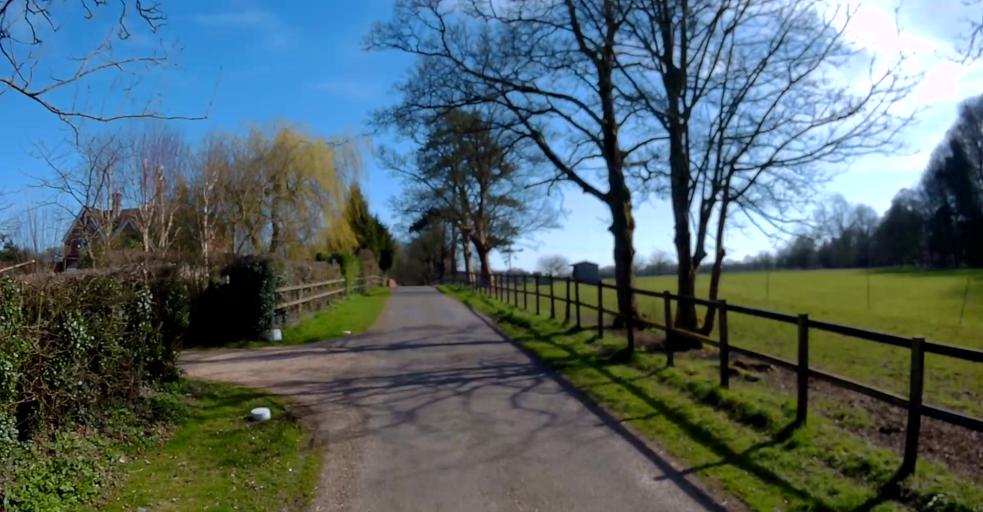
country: GB
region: England
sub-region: Hampshire
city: Four Marks
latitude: 51.1816
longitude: -1.0700
